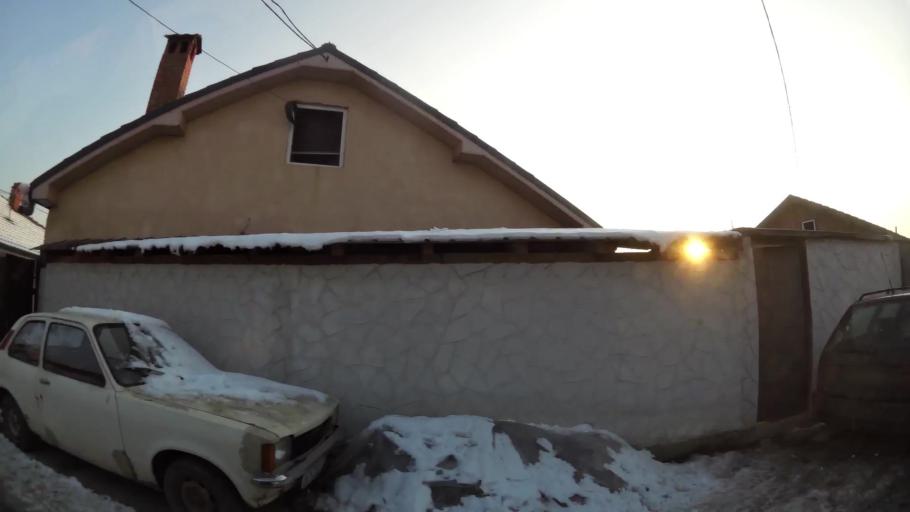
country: MK
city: Creshevo
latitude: 42.0148
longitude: 21.5155
